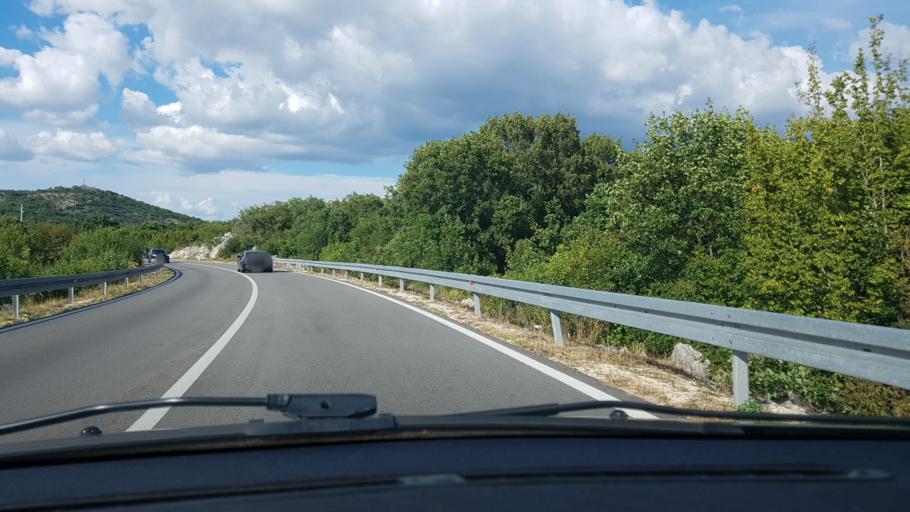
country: HR
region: Splitsko-Dalmatinska
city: Grubine
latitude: 43.4120
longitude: 17.0955
